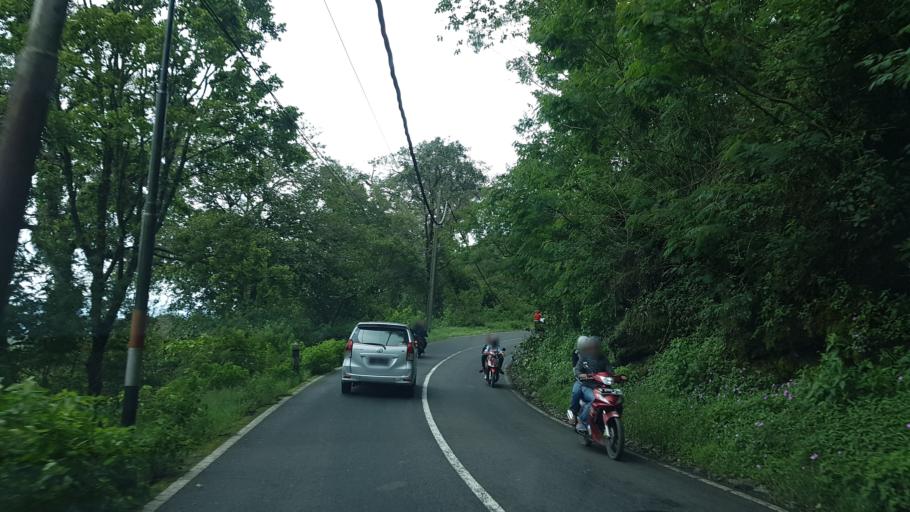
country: ID
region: West Java
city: Banjar
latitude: -7.1355
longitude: 107.4063
